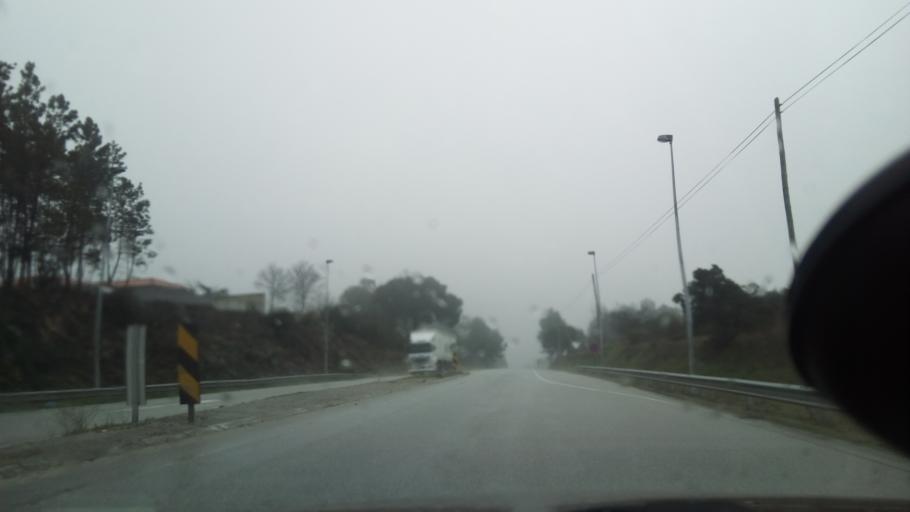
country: PT
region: Viseu
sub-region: Mangualde
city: Mangualde
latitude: 40.6053
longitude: -7.7827
